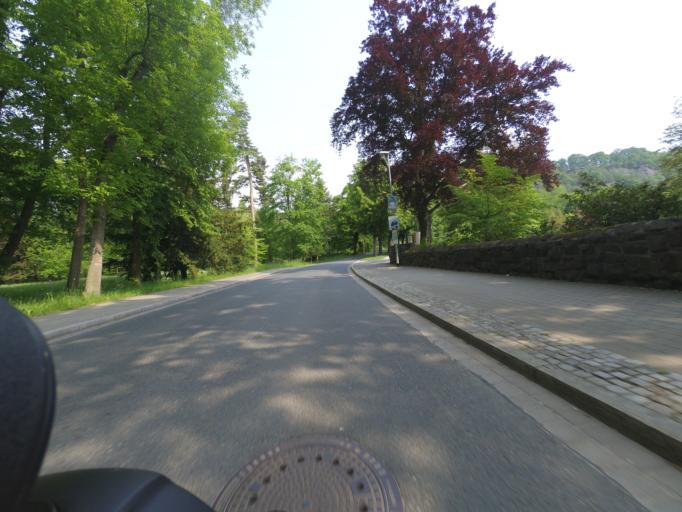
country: DE
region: Saxony
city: Rabenau
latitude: 50.9792
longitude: 13.6215
